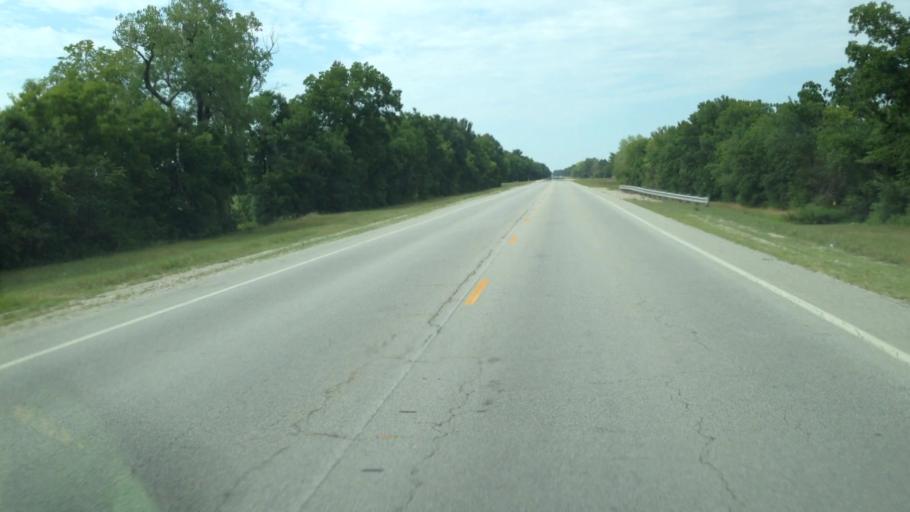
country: US
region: Kansas
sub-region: Labette County
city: Chetopa
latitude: 37.0594
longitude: -95.1027
